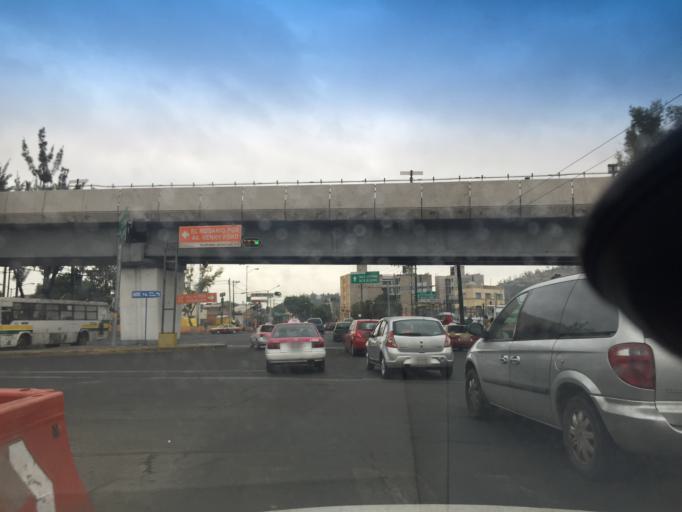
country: MX
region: Mexico City
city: Gustavo A. Madero
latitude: 19.4823
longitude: -99.1059
